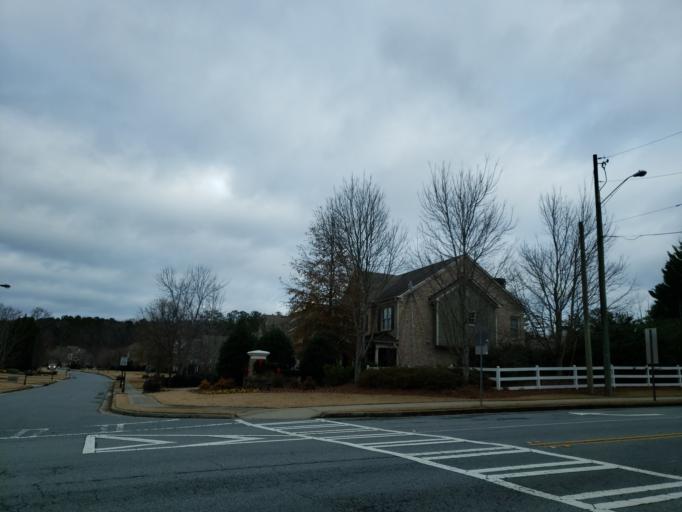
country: US
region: Georgia
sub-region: Cobb County
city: Fair Oaks
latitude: 33.9213
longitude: -84.6241
